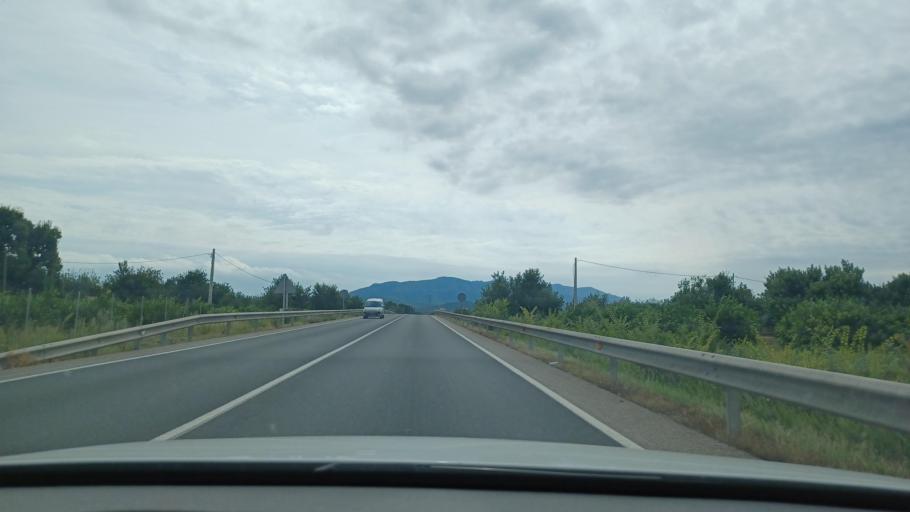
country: ES
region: Catalonia
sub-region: Provincia de Tarragona
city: Santa Barbara
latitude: 40.7225
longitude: 0.5041
